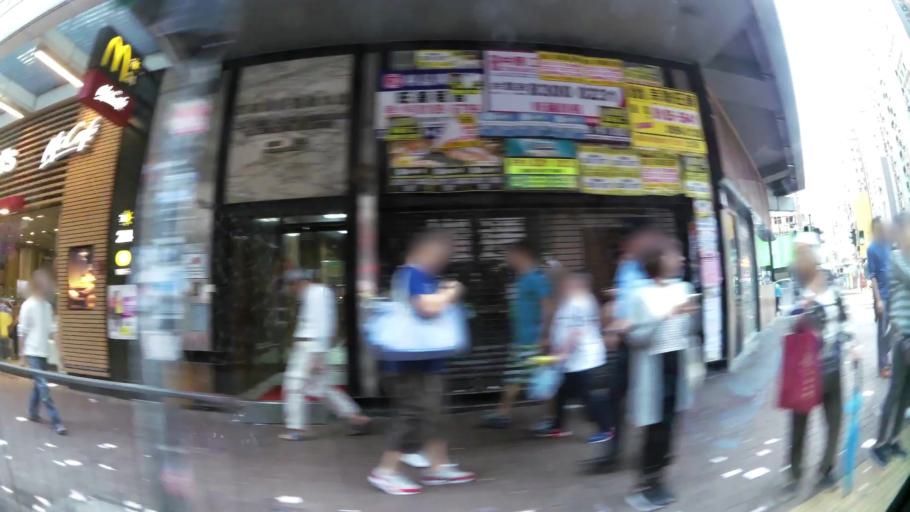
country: HK
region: Sham Shui Po
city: Sham Shui Po
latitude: 22.3199
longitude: 114.1656
